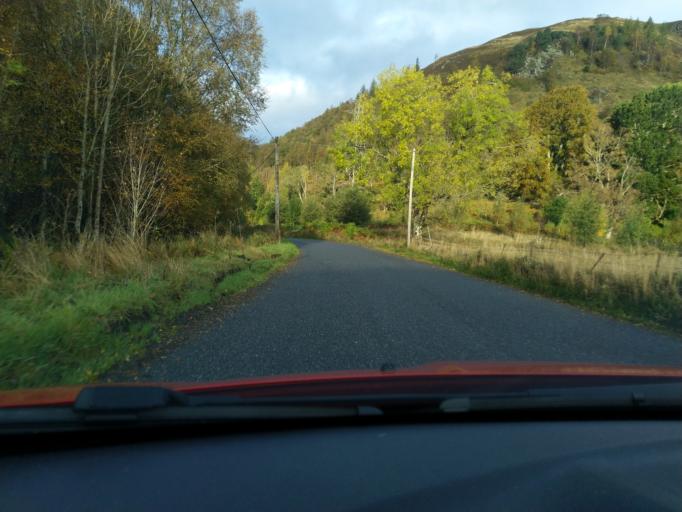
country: GB
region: Scotland
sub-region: Perth and Kinross
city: Aberfeldy
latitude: 56.7015
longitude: -4.1369
